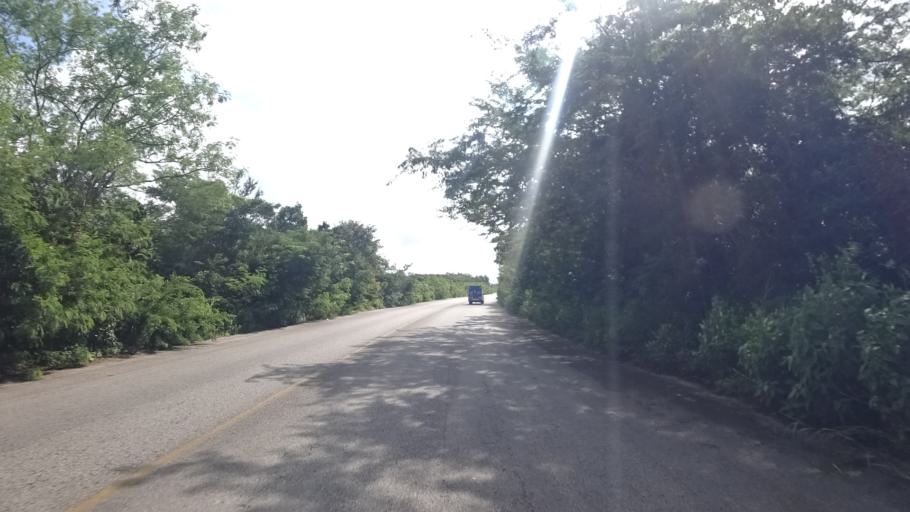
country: MX
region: Yucatan
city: Valladolid
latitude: 20.7251
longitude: -88.2148
